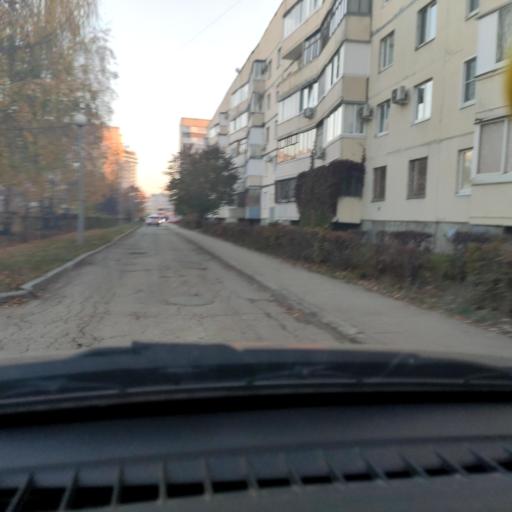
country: RU
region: Samara
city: Tol'yatti
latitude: 53.5372
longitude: 49.3411
